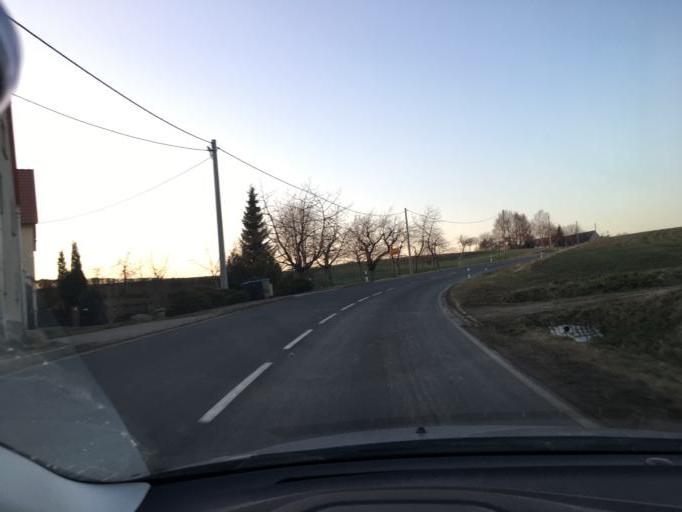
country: DE
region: Saxony
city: Lunzenau
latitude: 50.9668
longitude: 12.7485
